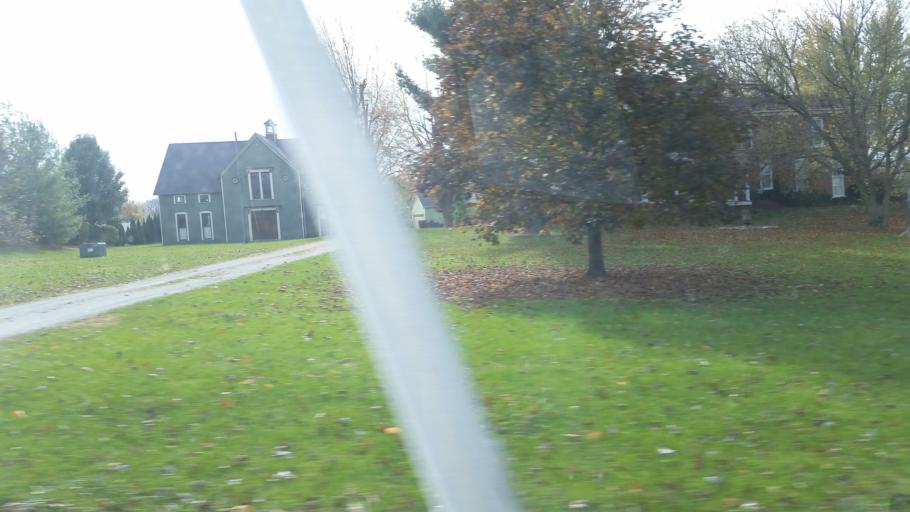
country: US
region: Indiana
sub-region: Howard County
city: Indian Heights
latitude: 40.4332
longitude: -86.1340
